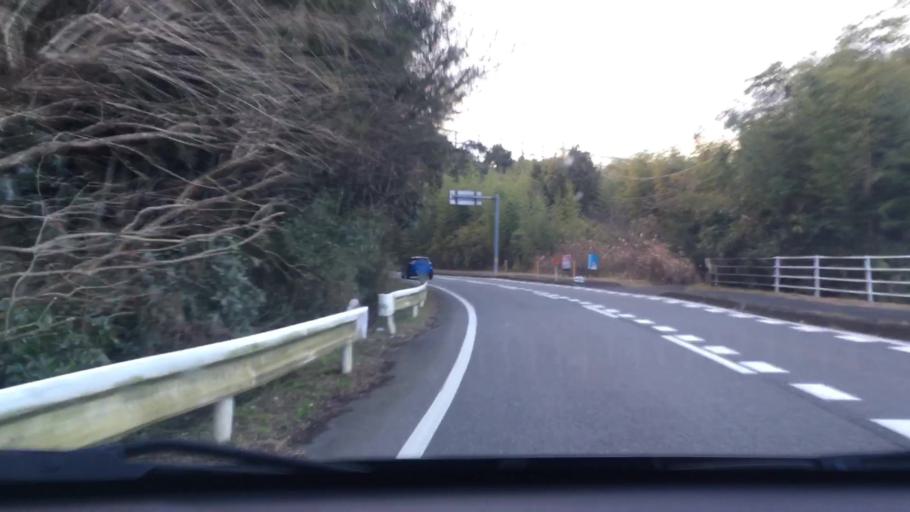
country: JP
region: Oita
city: Hiji
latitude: 33.3735
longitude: 131.4576
